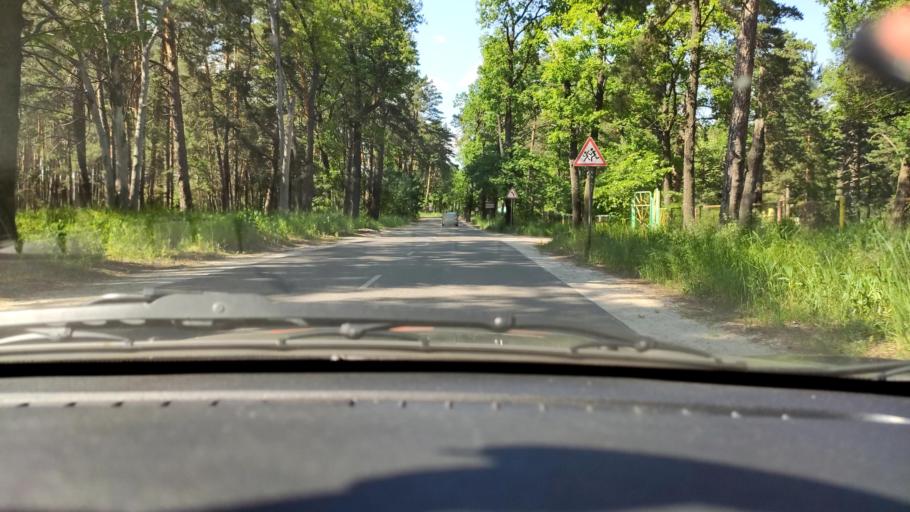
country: RU
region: Voronezj
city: Somovo
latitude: 51.7576
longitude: 39.3661
